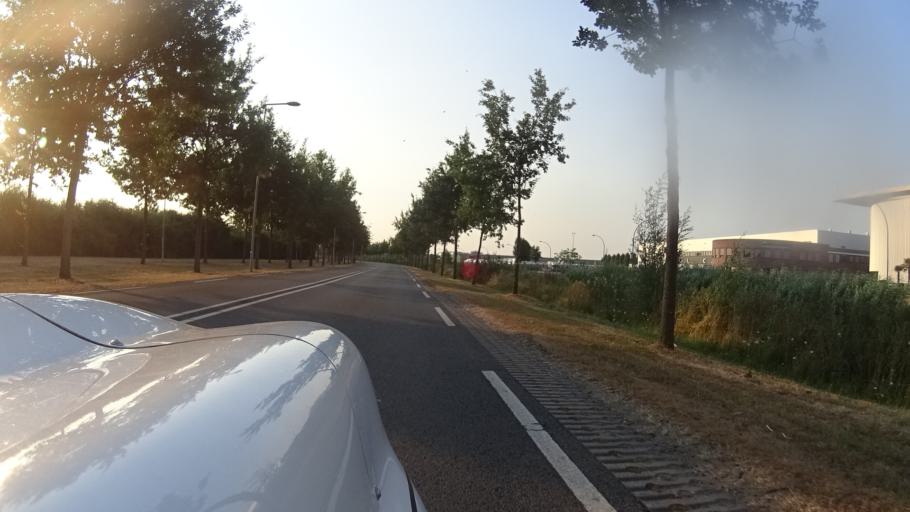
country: NL
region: Gelderland
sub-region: Gemeente Tiel
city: Tiel
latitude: 51.9109
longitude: 5.4506
